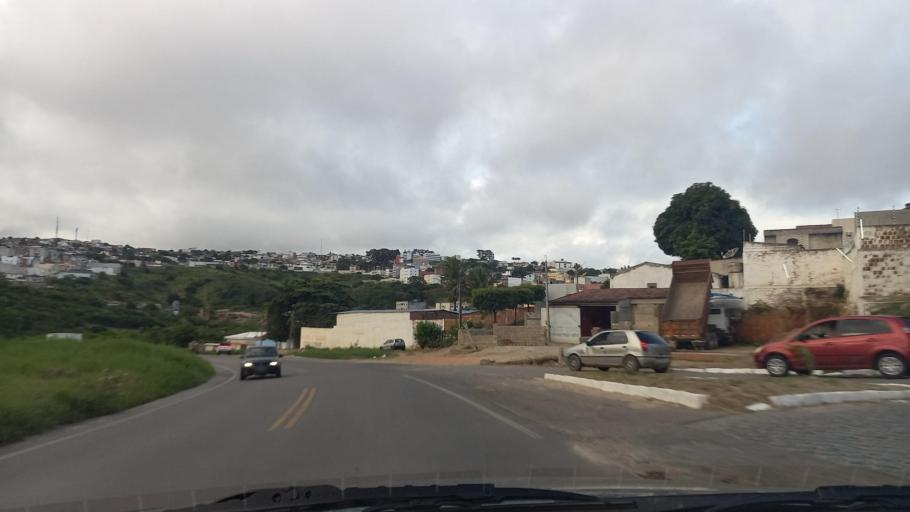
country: BR
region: Pernambuco
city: Garanhuns
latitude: -8.8950
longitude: -36.5004
